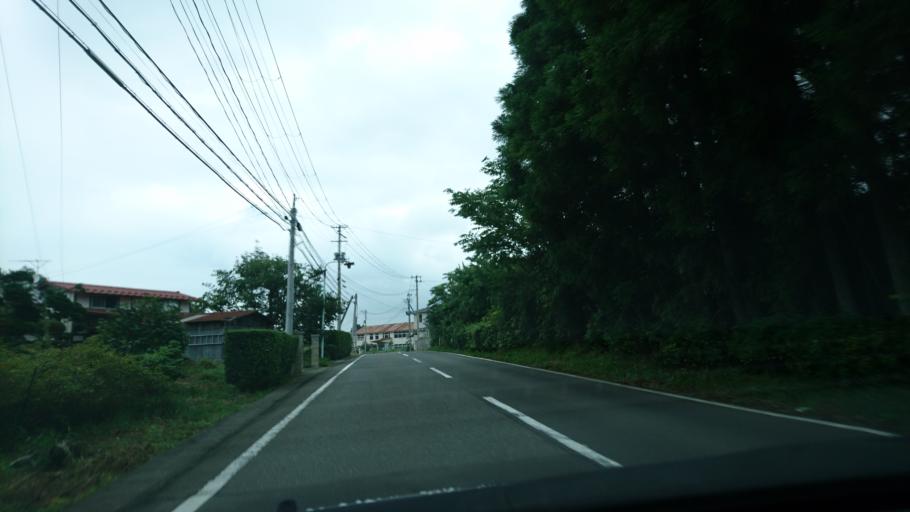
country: JP
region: Iwate
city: Ichinoseki
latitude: 38.8052
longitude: 140.9425
